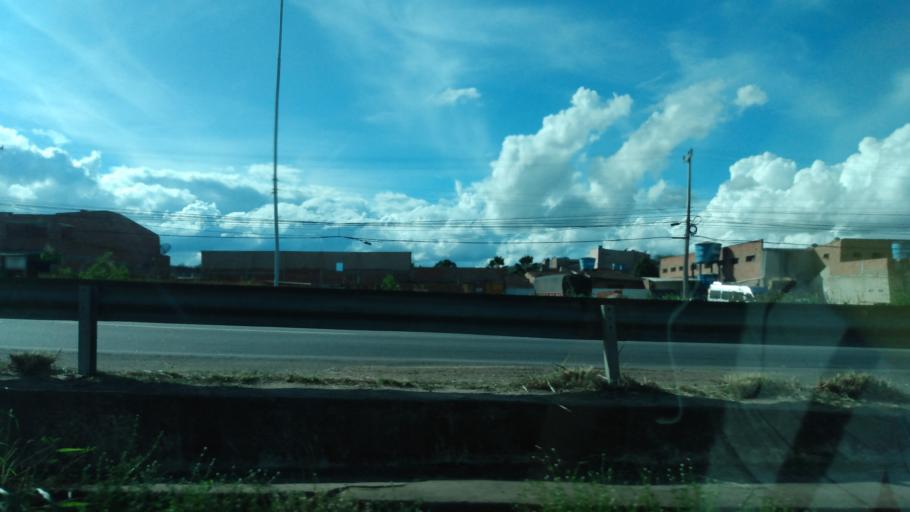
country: ET
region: Oromiya
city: Gore
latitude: 8.1968
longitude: 35.5766
